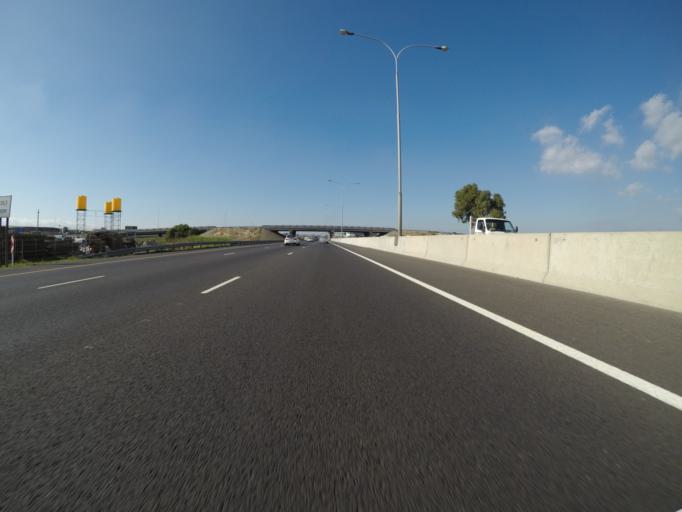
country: ZA
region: Western Cape
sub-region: City of Cape Town
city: Kraaifontein
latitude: -33.9090
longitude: 18.6716
